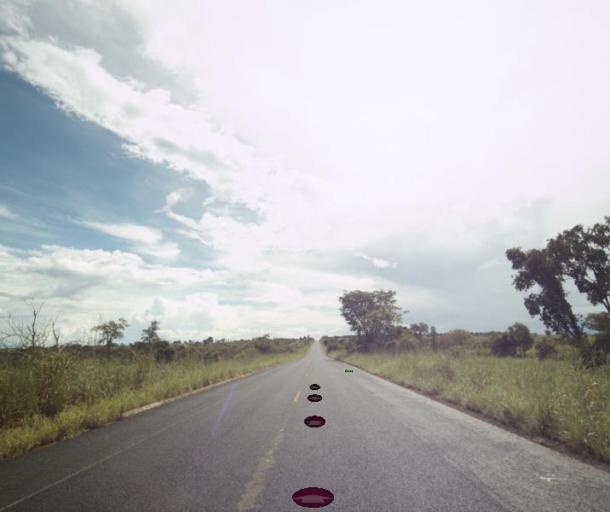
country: BR
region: Goias
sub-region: Sao Miguel Do Araguaia
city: Sao Miguel do Araguaia
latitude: -13.3013
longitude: -50.2886
